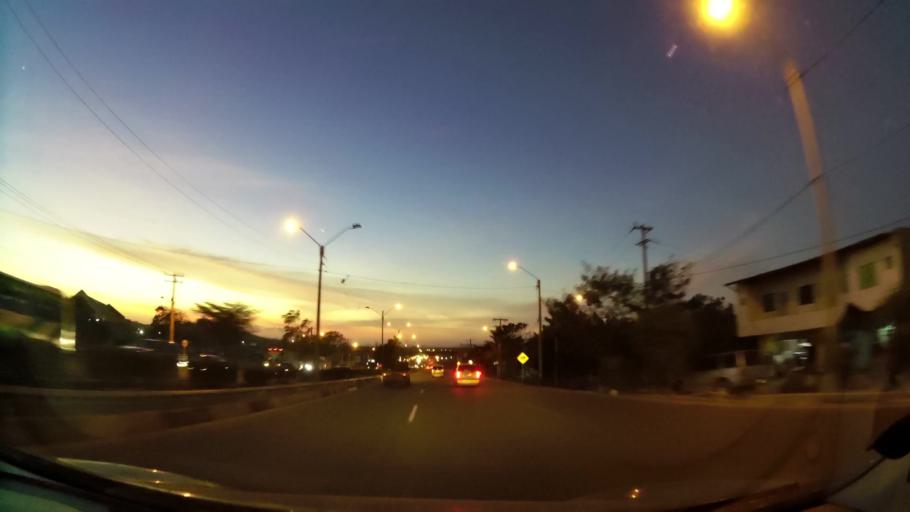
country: CO
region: Atlantico
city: Soledad
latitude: 10.9242
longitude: -74.8193
